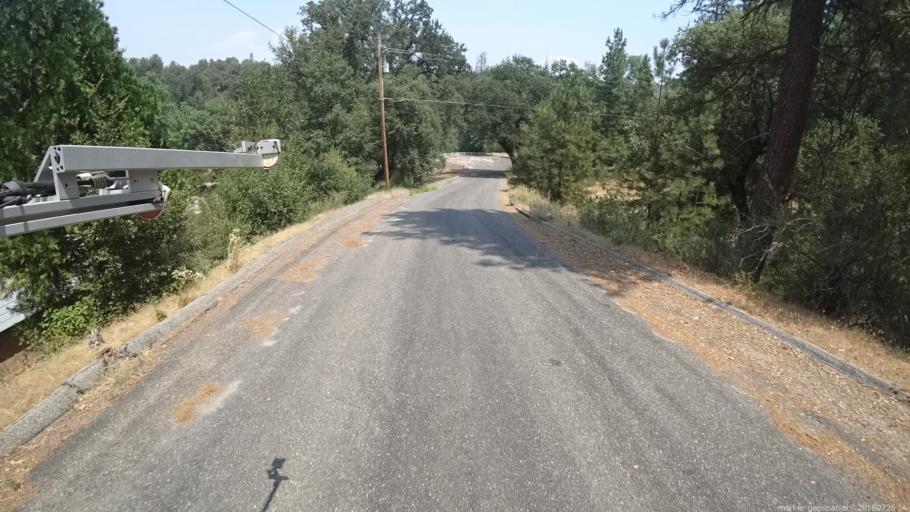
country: US
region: California
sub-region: Madera County
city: Oakhurst
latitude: 37.3095
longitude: -119.6389
